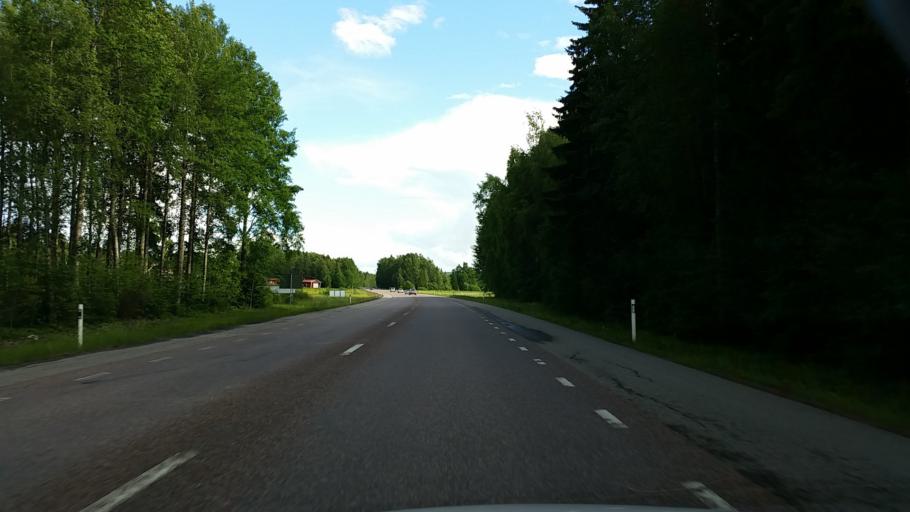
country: SE
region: Dalarna
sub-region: Smedjebackens Kommun
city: Smedjebacken
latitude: 60.0690
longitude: 15.5473
